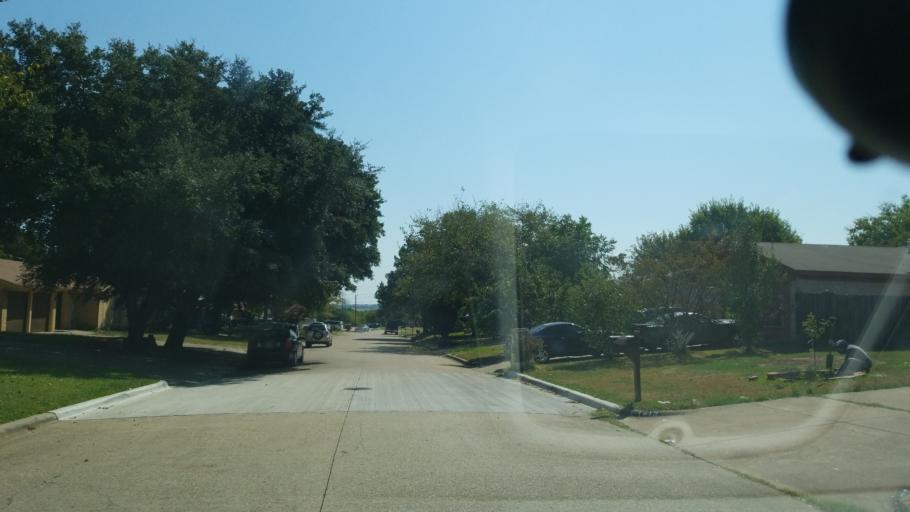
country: US
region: Texas
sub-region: Dallas County
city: Grand Prairie
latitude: 32.7063
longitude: -96.9832
